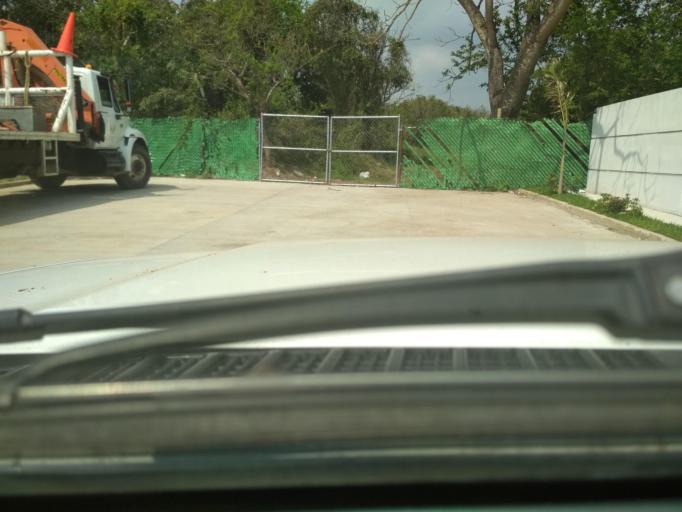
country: MX
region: Veracruz
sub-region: Veracruz
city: Lomas de Rio Medio Cuatro
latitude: 19.1815
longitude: -96.2094
